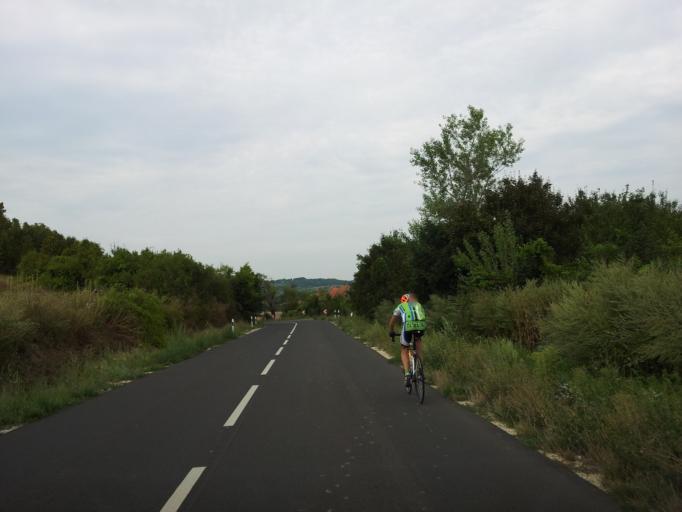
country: HU
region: Veszprem
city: Balatonfured
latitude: 46.9461
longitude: 17.7797
